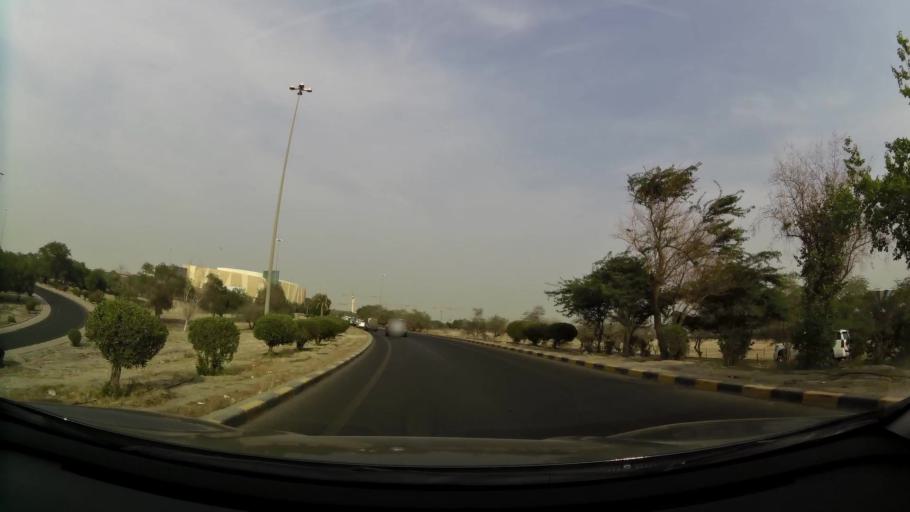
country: KW
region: Al Farwaniyah
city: Janub as Surrah
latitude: 29.2639
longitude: 47.9896
